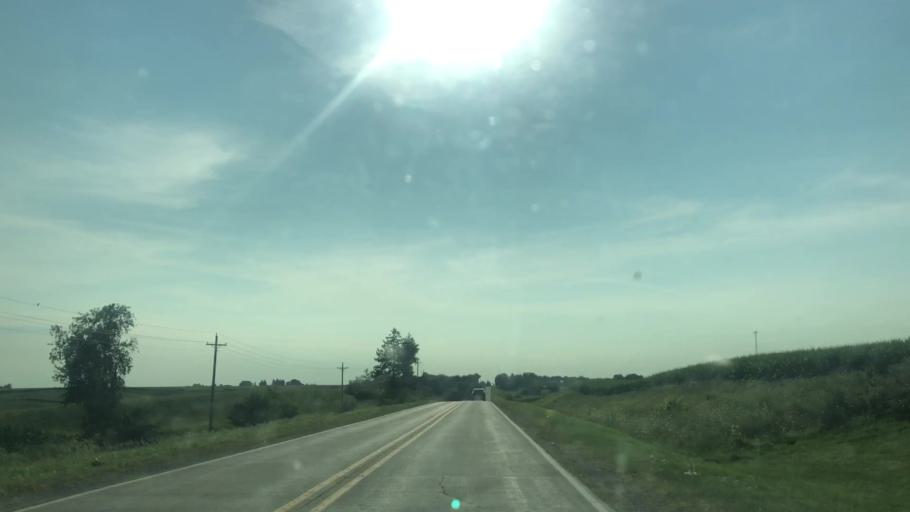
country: US
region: Iowa
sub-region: Marshall County
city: Marshalltown
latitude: 42.0488
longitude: -92.9944
